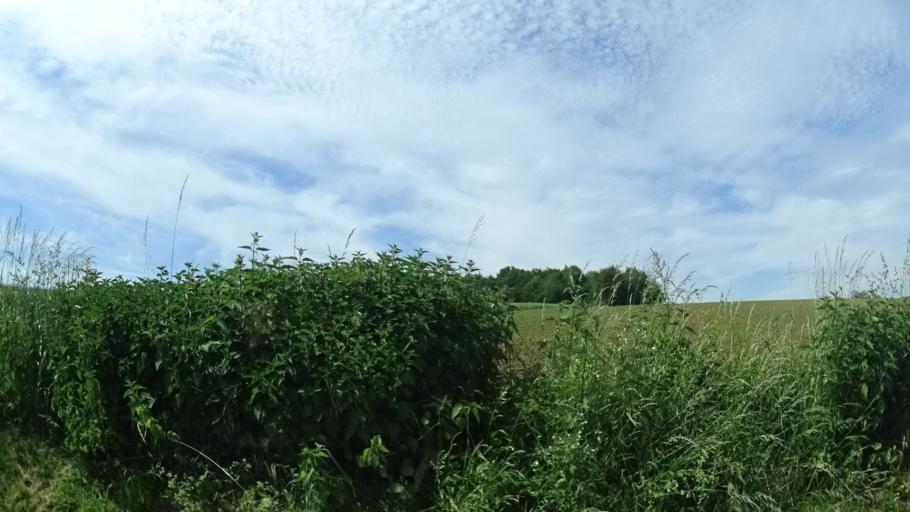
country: DE
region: Bavaria
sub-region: Regierungsbezirk Unterfranken
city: Birkenfeld
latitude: 49.8652
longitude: 9.7101
